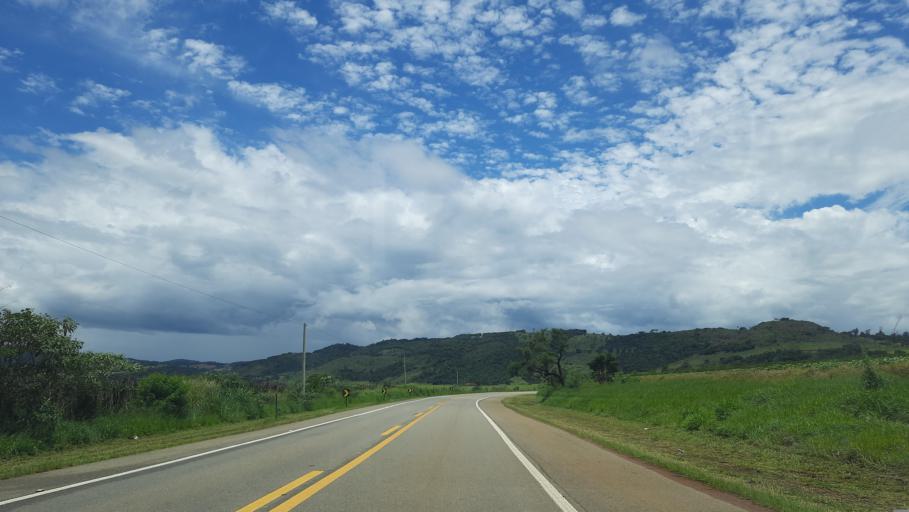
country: BR
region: Sao Paulo
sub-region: Vargem Grande Do Sul
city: Vargem Grande do Sul
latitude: -21.8142
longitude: -46.7862
